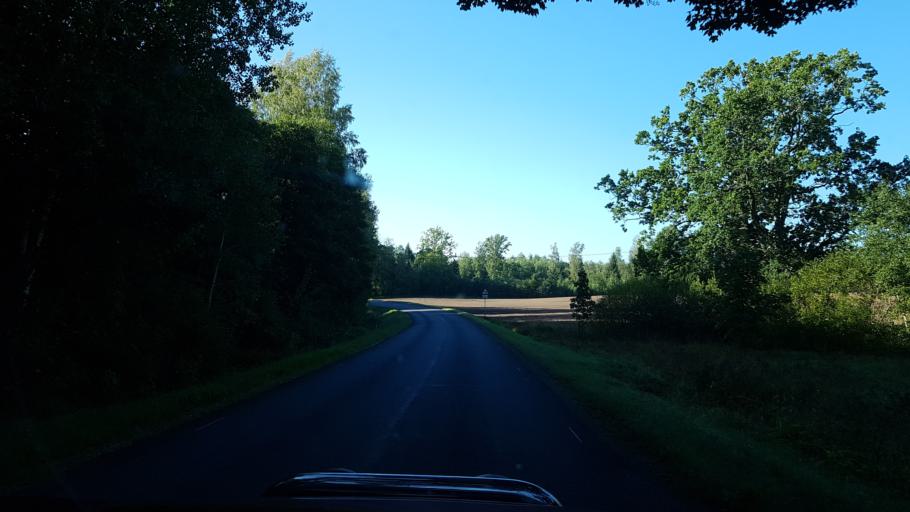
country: EE
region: Jogevamaa
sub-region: Jogeva linn
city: Jogeva
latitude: 58.7274
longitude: 26.5168
